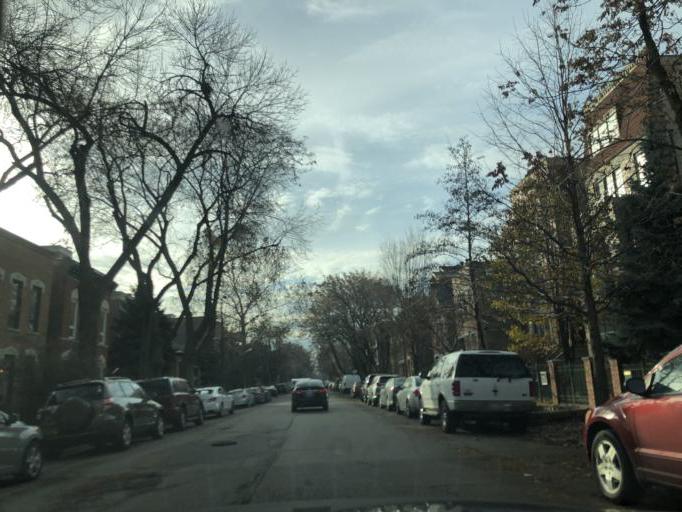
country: US
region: Illinois
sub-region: Cook County
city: Chicago
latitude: 41.9010
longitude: -87.6748
